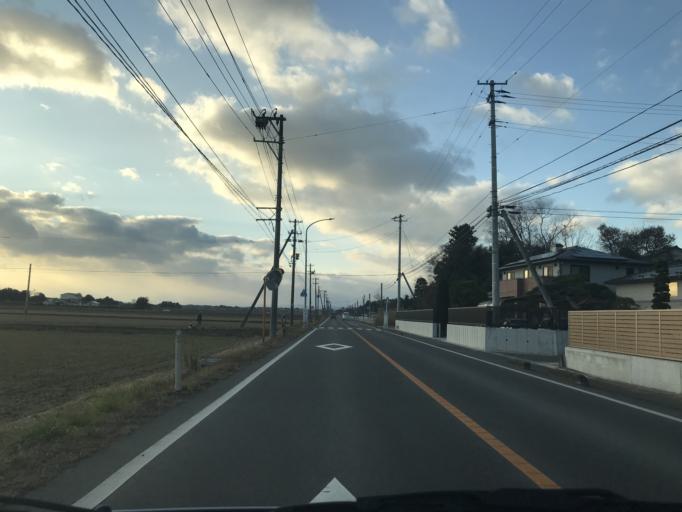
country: JP
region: Miyagi
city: Kogota
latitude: 38.6540
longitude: 141.0512
